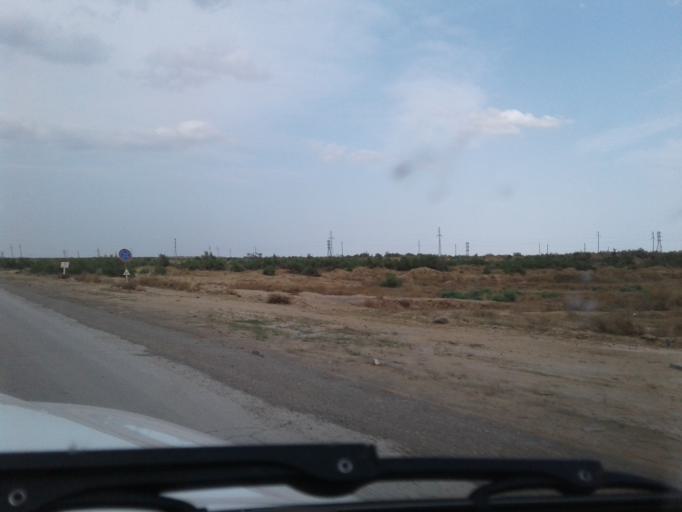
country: TM
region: Mary
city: Mary
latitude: 37.3205
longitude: 61.4073
